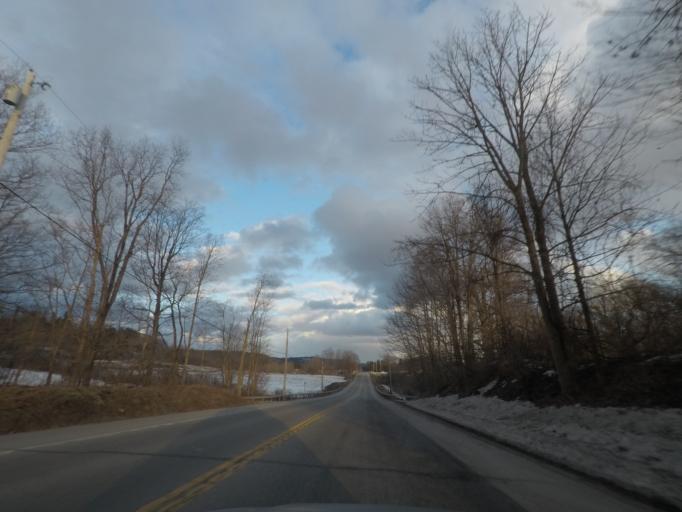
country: US
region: New York
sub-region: Montgomery County
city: Saint Johnsville
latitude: 43.0049
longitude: -74.7214
